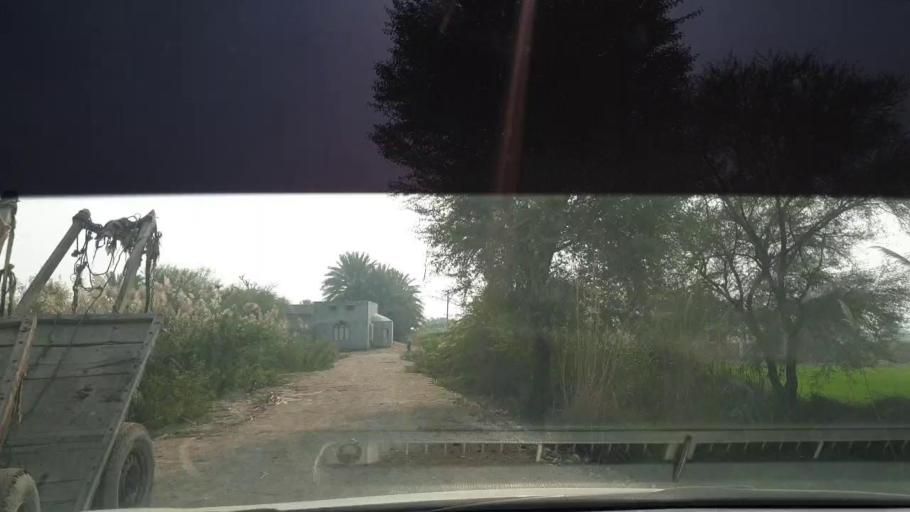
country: PK
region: Sindh
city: Berani
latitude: 25.8471
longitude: 68.8447
